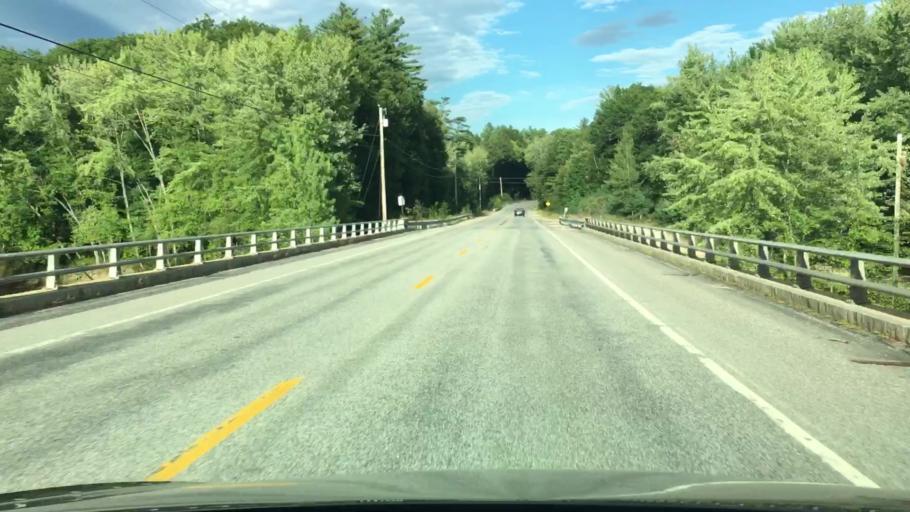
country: US
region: Maine
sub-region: Oxford County
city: Fryeburg
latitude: 44.0290
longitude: -70.9207
